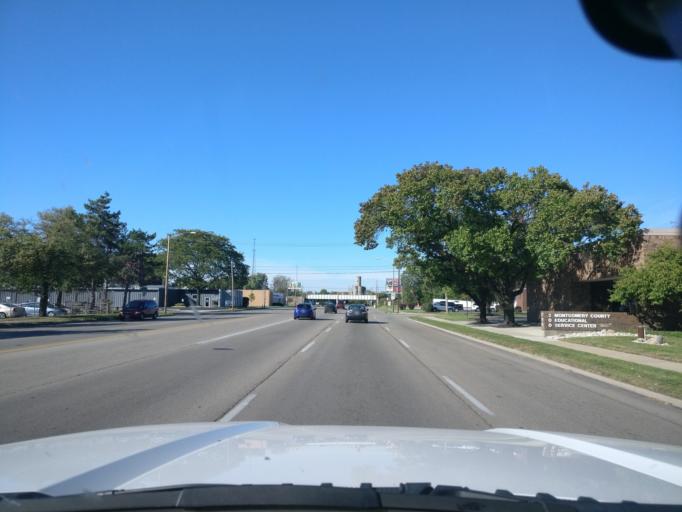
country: US
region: Ohio
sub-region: Montgomery County
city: Dayton
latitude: 39.7589
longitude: -84.1773
